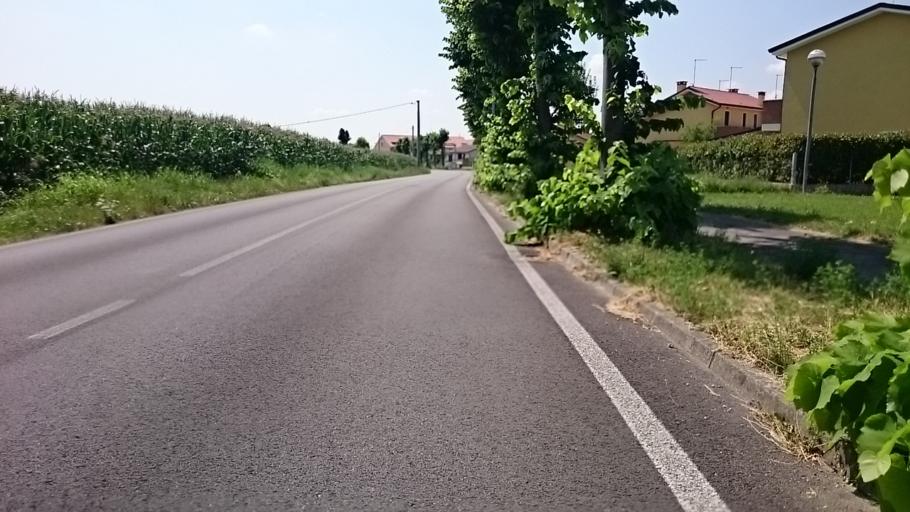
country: IT
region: Veneto
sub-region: Provincia di Padova
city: Terradura
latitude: 45.3268
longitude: 11.8253
